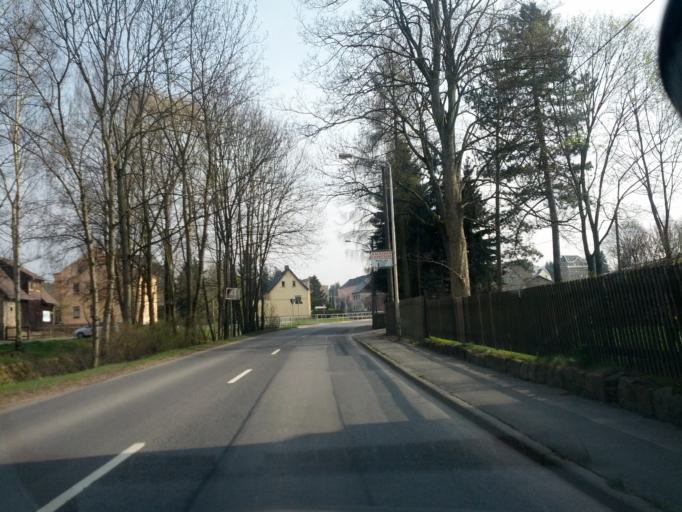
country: DE
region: Saxony
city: Kirchberg
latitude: 50.6124
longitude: 12.5405
